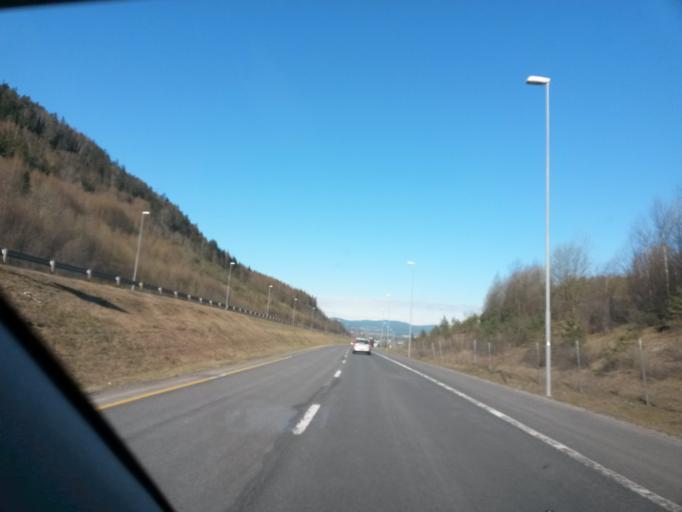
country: NO
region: Buskerud
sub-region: Nedre Eiker
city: Mjondalen
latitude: 59.7460
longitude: 10.0629
